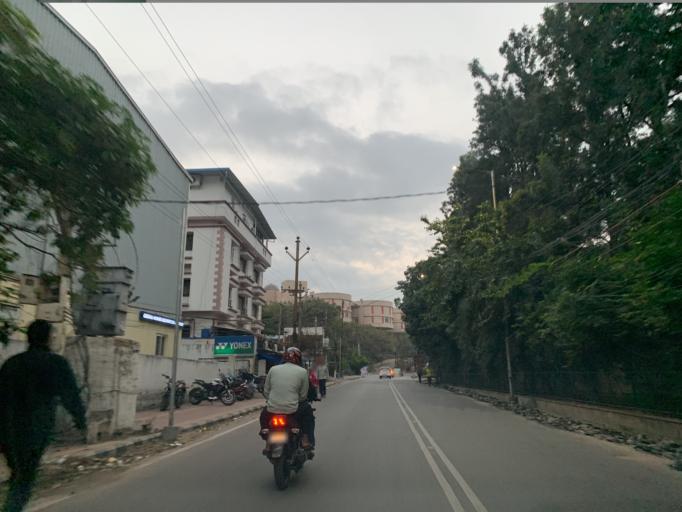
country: IN
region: Telangana
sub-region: Rangareddi
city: Kukatpalli
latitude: 17.4366
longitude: 78.3964
